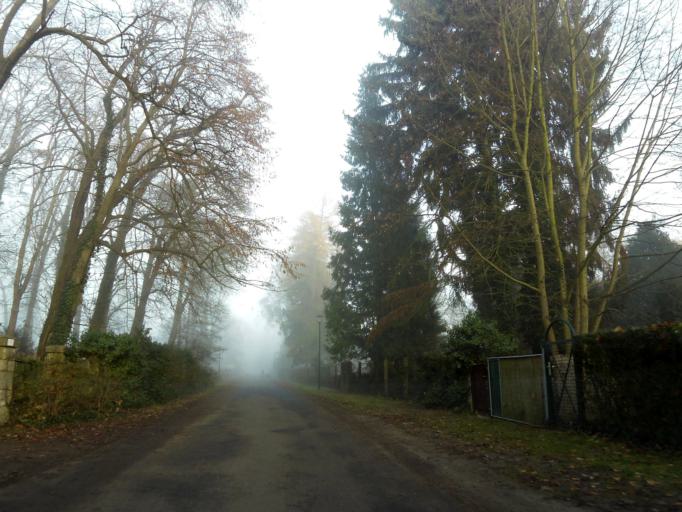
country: DE
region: Brandenburg
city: Werder
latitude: 52.3571
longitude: 12.9853
